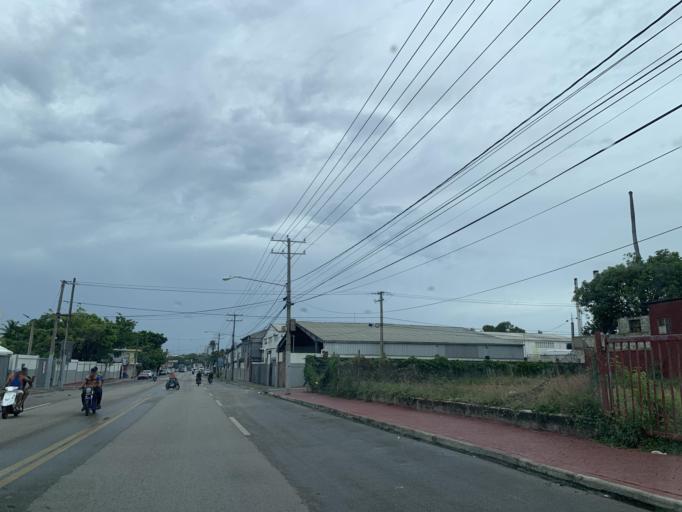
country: DO
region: Puerto Plata
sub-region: Puerto Plata
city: Puerto Plata
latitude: 19.7938
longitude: -70.6993
